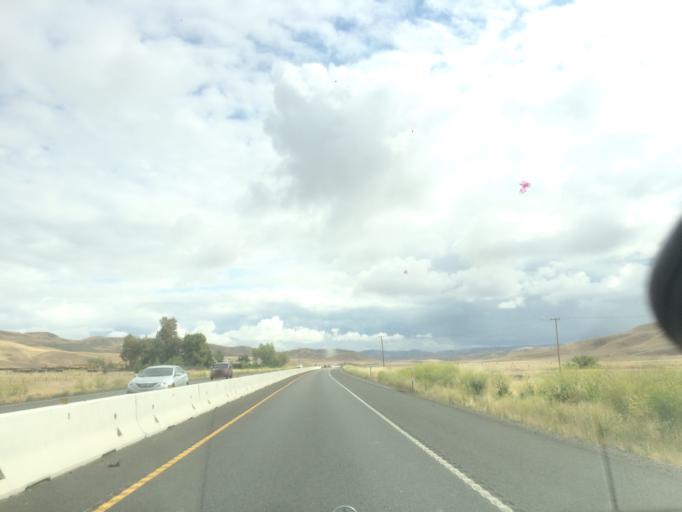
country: US
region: California
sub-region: San Luis Obispo County
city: Shandon
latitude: 35.6942
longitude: -120.3303
